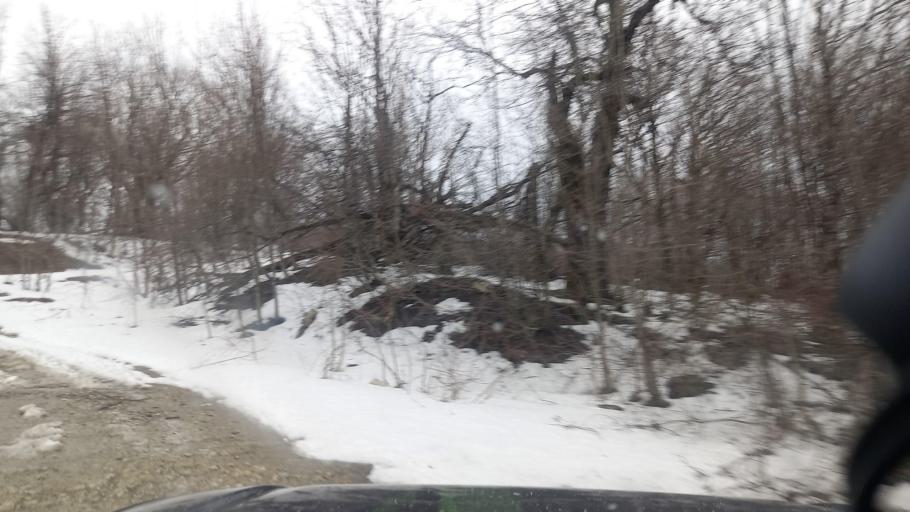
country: RU
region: Krasnodarskiy
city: Pshada
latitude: 44.5966
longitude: 38.3246
